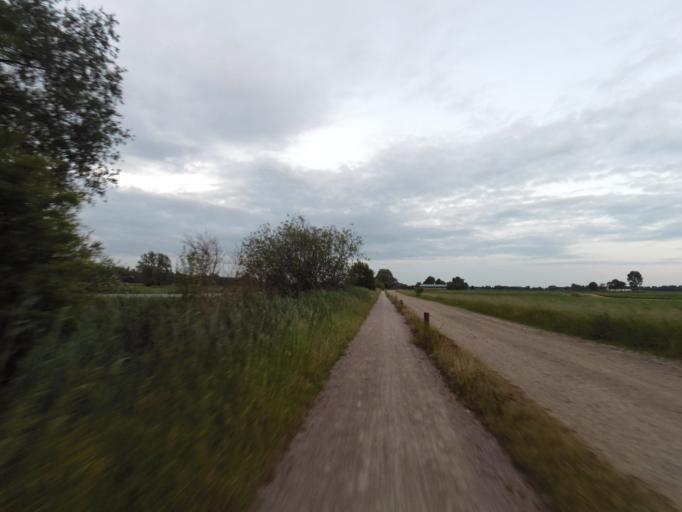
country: NL
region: Gelderland
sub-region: Gemeente Zevenaar
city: Zevenaar
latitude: 51.8804
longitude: 6.1327
